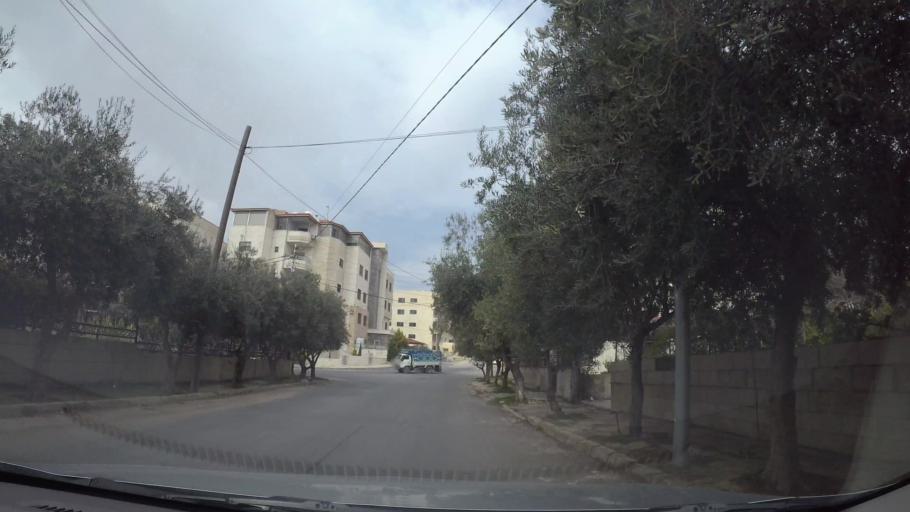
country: JO
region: Amman
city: Umm as Summaq
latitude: 31.8900
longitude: 35.8601
